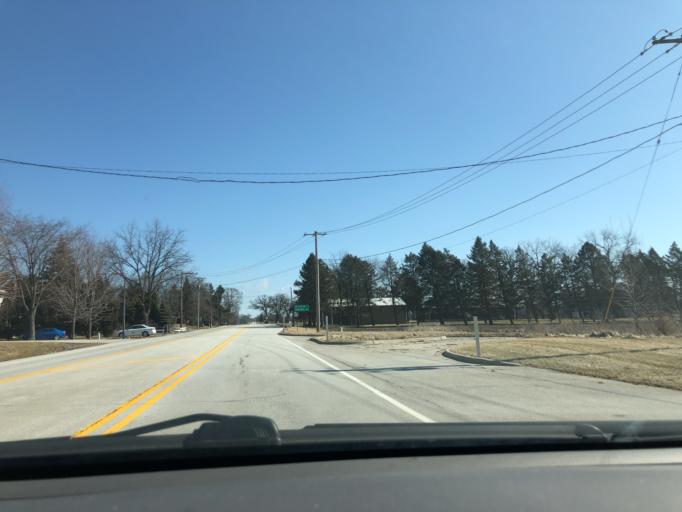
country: US
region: Illinois
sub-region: Kane County
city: Hampshire
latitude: 42.1064
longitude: -88.5328
